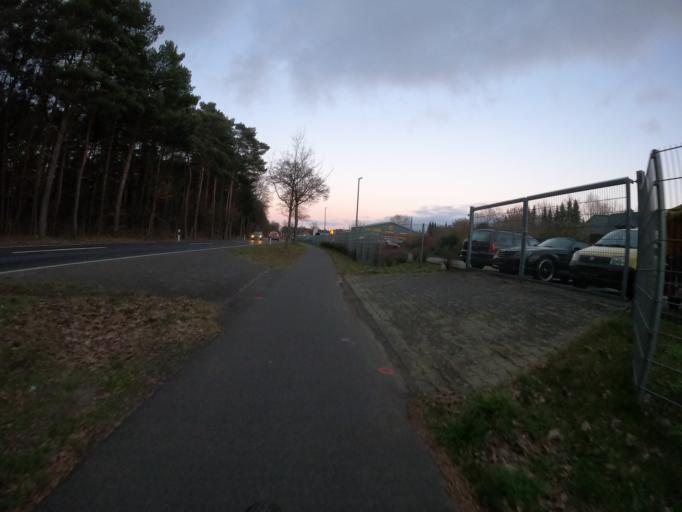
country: DE
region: Lower Saxony
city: Haselunne
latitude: 52.6628
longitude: 7.4578
